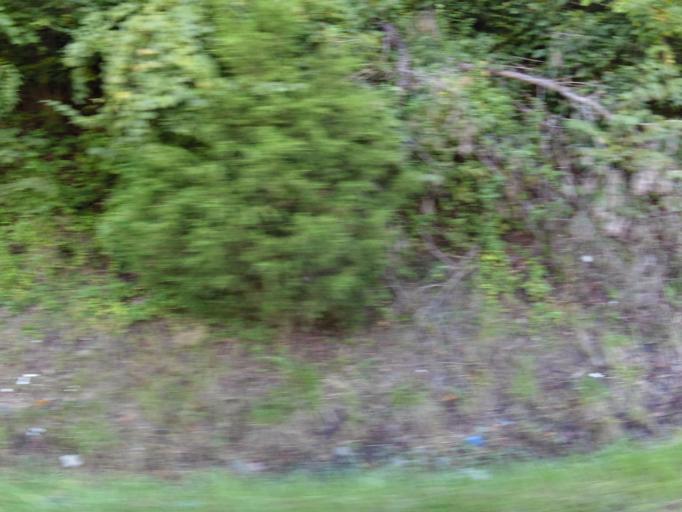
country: US
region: Kentucky
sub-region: Whitley County
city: Williamsburg
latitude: 36.7442
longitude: -84.1561
